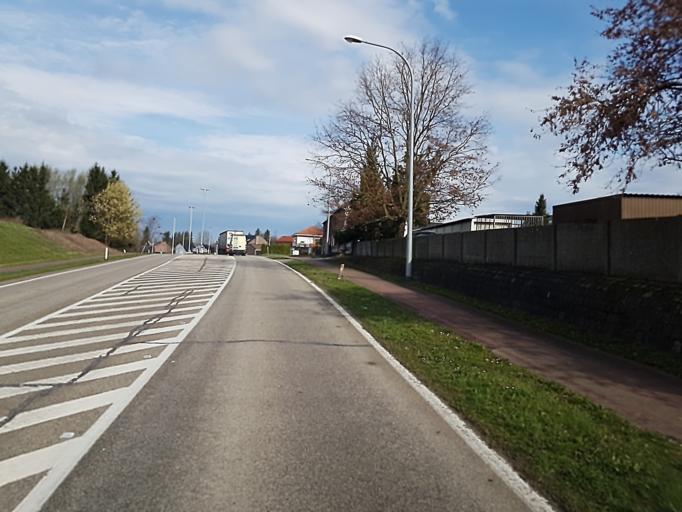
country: BE
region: Flanders
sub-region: Provincie Limburg
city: Tongeren
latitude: 50.7976
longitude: 5.4480
